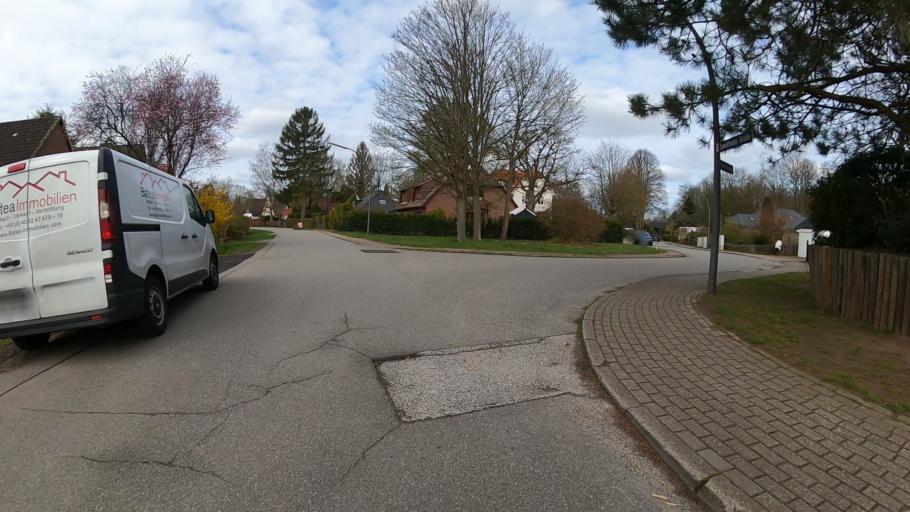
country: DE
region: Hamburg
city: Sasel
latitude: 53.6360
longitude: 10.1433
